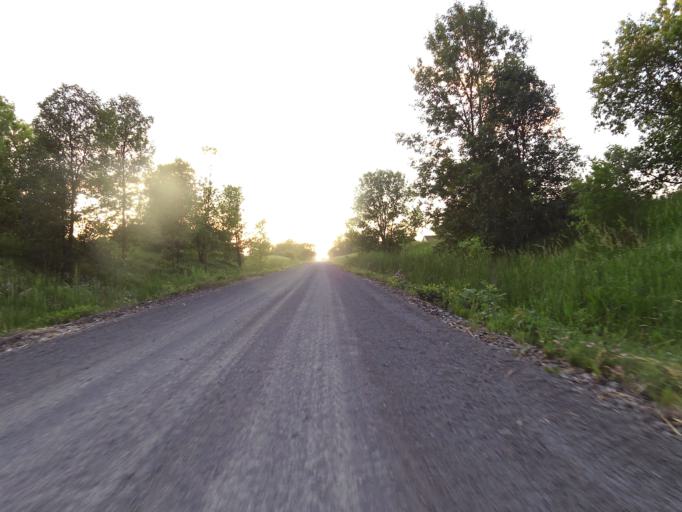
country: CA
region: Ontario
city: Arnprior
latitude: 45.4075
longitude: -76.3304
